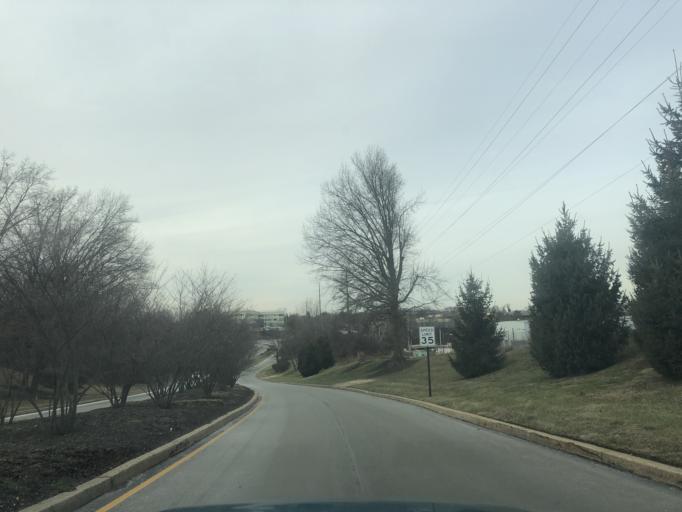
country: US
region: Pennsylvania
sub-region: Montgomery County
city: West Conshohocken
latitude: 40.0802
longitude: -75.3322
